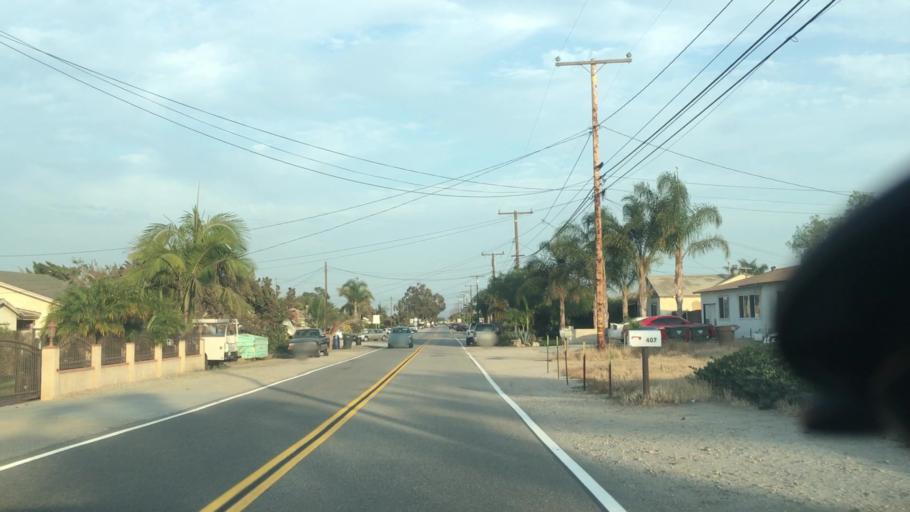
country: US
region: California
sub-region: Ventura County
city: El Rio
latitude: 34.2387
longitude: -119.1630
